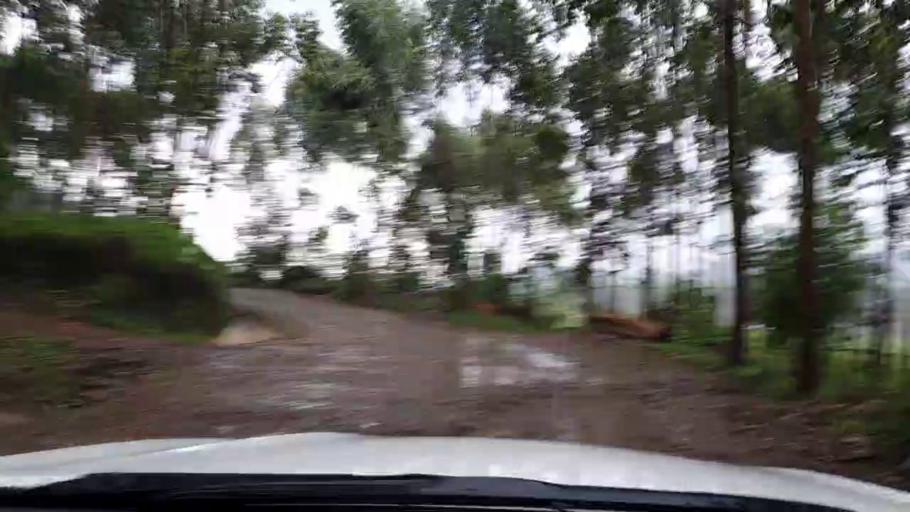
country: RW
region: Western Province
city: Cyangugu
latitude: -2.4732
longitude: 29.0333
